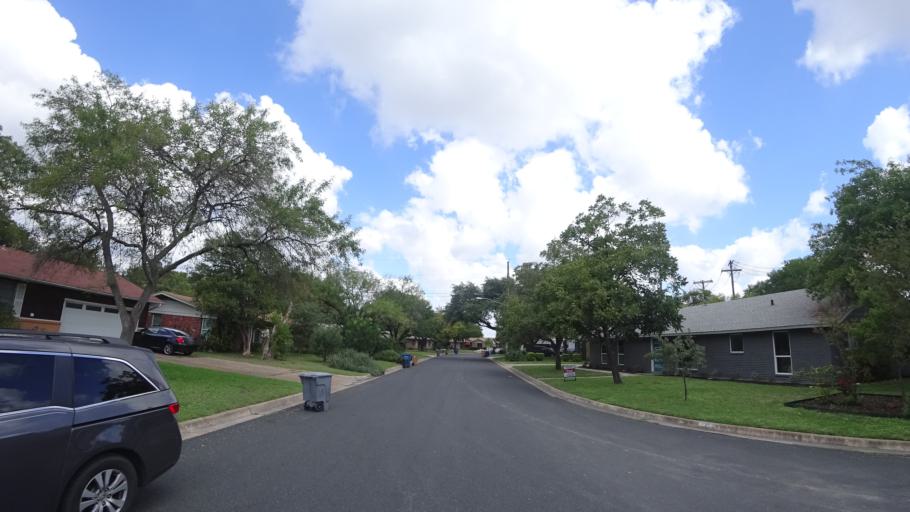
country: US
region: Texas
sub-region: Travis County
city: Austin
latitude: 30.3571
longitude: -97.7193
